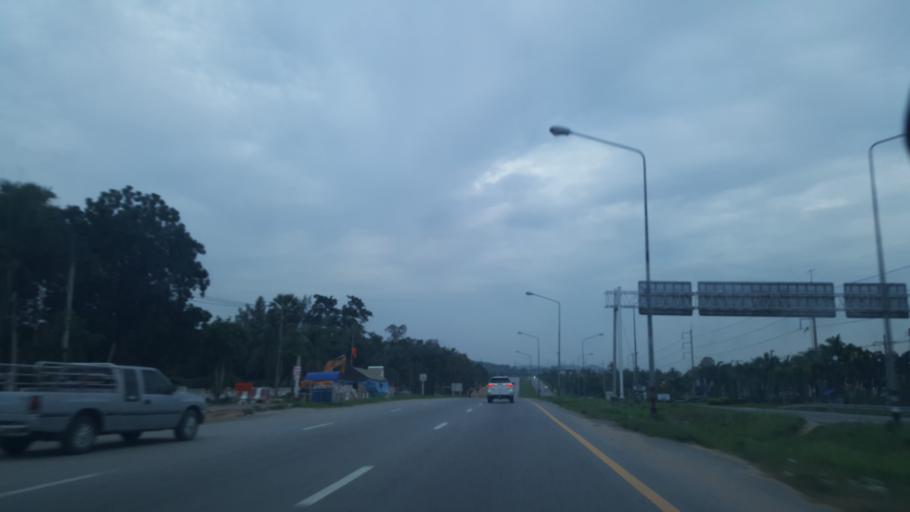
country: TH
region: Chon Buri
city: Ban Talat Bueng
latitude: 12.9516
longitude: 101.0469
